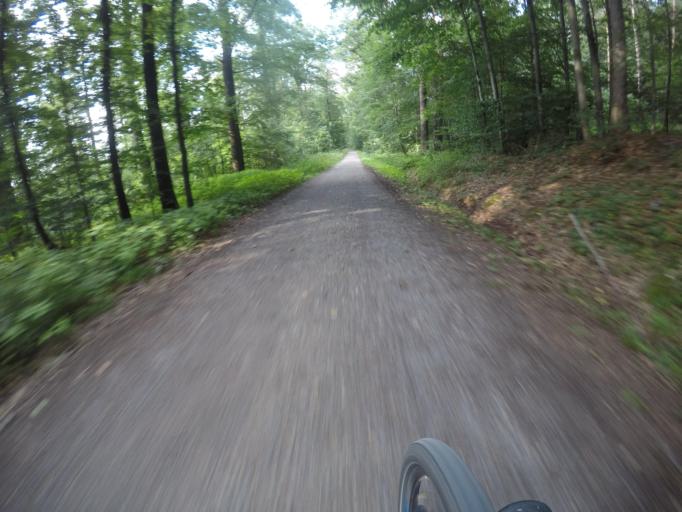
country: DE
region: Baden-Wuerttemberg
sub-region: Regierungsbezirk Stuttgart
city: Ostfildern
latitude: 48.7460
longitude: 9.2505
